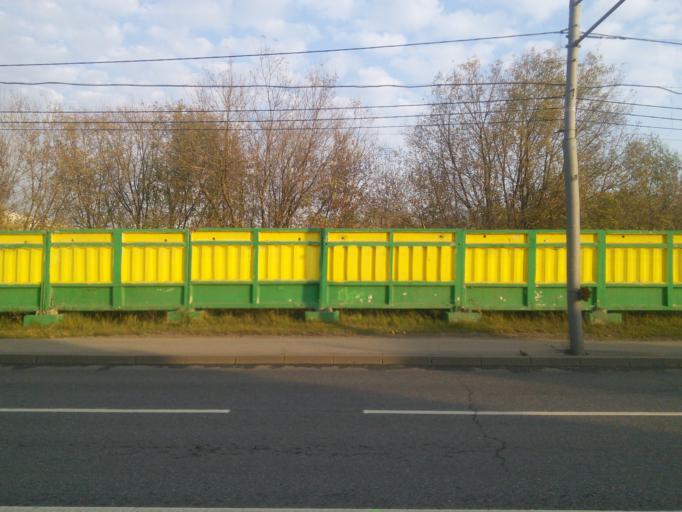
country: RU
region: Moskovskaya
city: Fili
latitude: 55.7585
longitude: 37.4650
